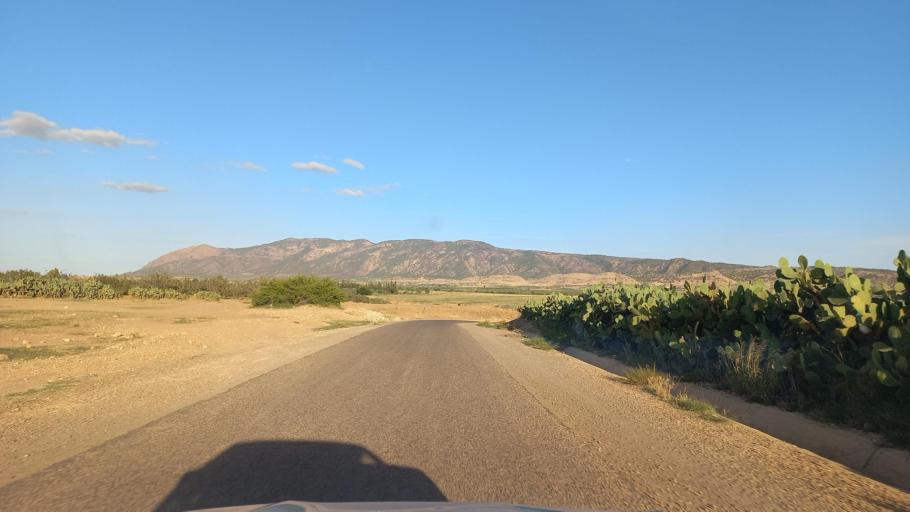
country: TN
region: Al Qasrayn
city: Sbiba
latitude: 35.4114
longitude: 9.1439
